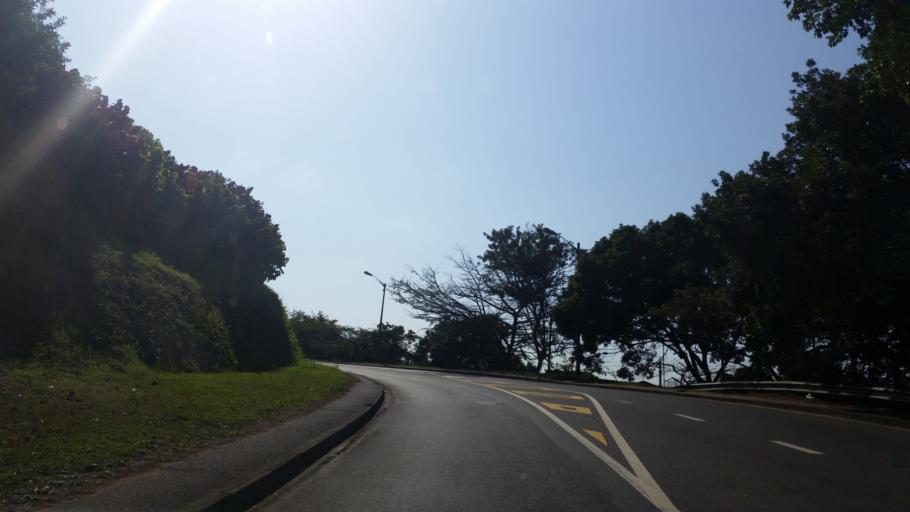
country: ZA
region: KwaZulu-Natal
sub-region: eThekwini Metropolitan Municipality
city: Berea
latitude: -29.8281
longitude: 30.9131
